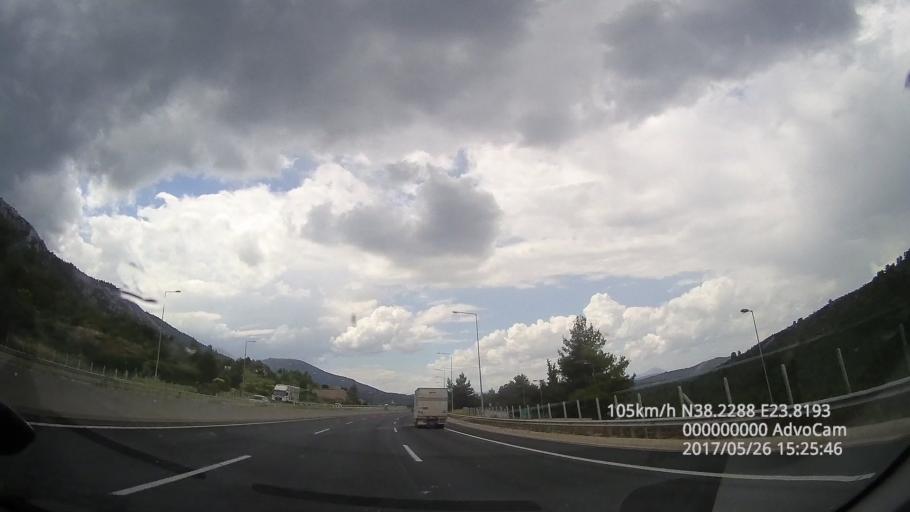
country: GR
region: Central Greece
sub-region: Nomos Voiotias
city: Akraifnia
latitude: 38.4613
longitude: 23.1639
